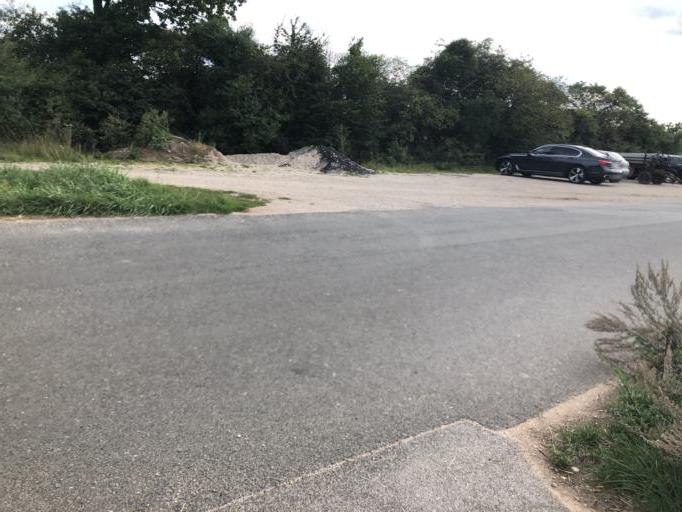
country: DE
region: Bavaria
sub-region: Regierungsbezirk Mittelfranken
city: Obermichelbach
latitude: 49.5409
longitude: 10.9665
